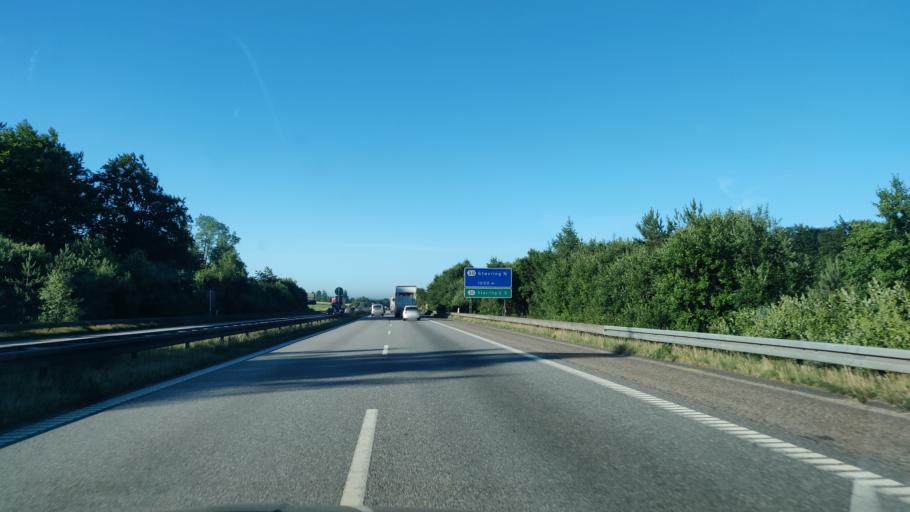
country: DK
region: North Denmark
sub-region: Rebild Kommune
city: Stovring
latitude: 56.9183
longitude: 9.8424
